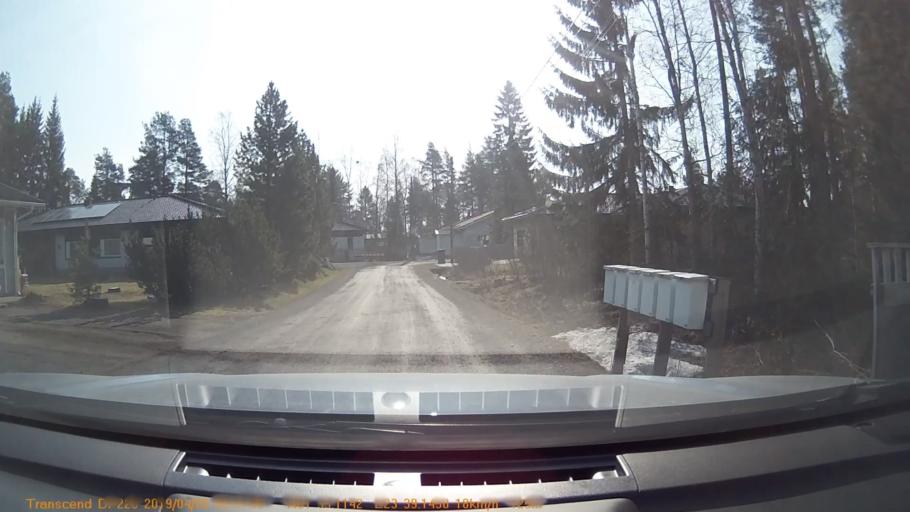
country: FI
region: Pirkanmaa
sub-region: Tampere
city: Yloejaervi
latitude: 61.5519
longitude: 23.6526
